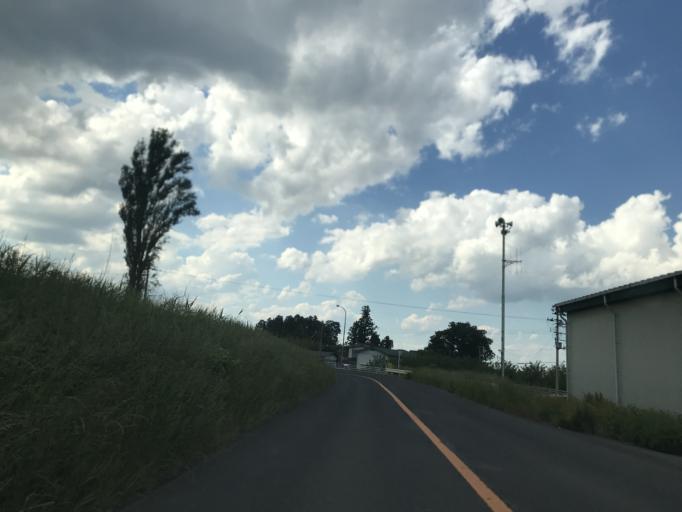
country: JP
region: Miyagi
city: Wakuya
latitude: 38.6689
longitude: 141.2120
